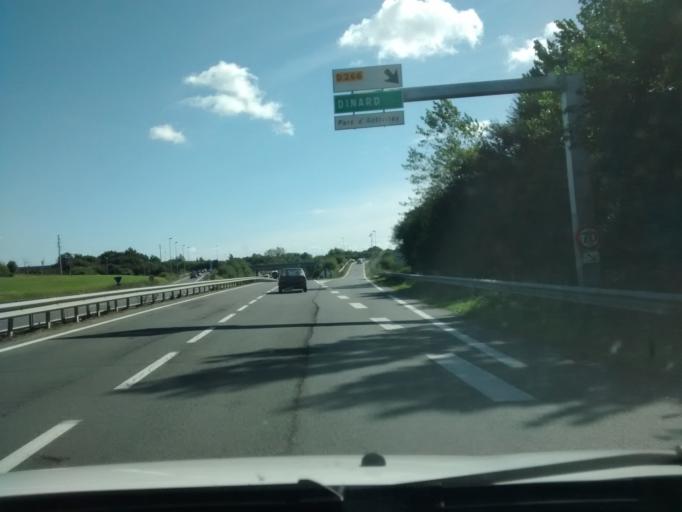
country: FR
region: Brittany
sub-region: Departement d'Ille-et-Vilaine
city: Dinard
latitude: 48.6134
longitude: -2.0617
